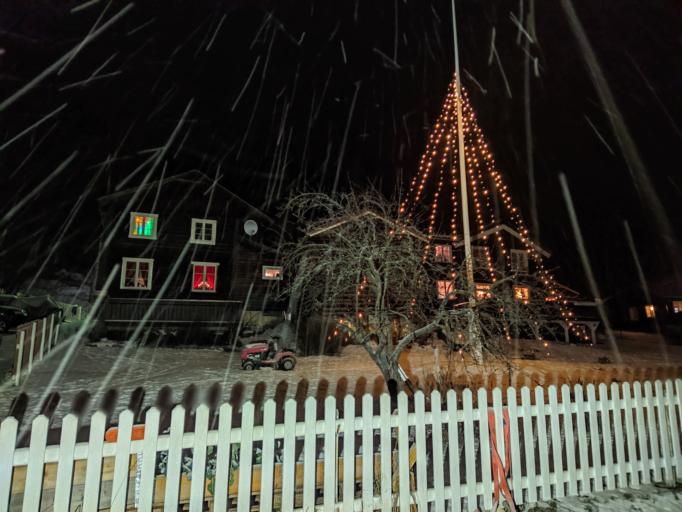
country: NO
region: Oppland
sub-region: Sel
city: Otta
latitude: 61.6833
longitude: 9.5203
